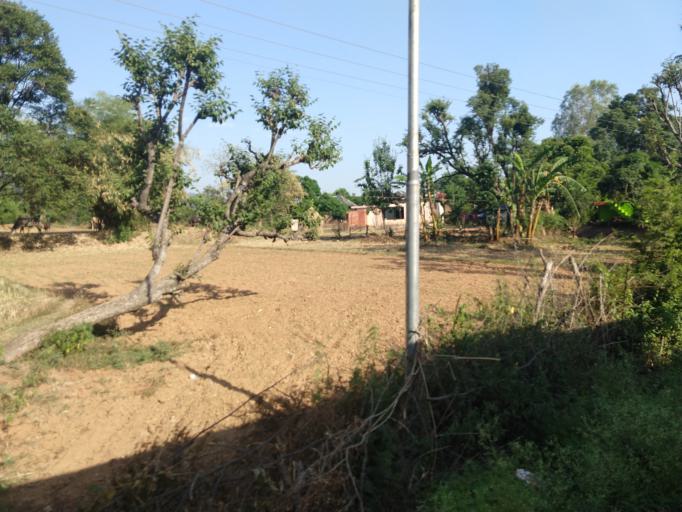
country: IN
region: Himachal Pradesh
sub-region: Chamba
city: Chowari
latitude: 32.3677
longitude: 75.9213
